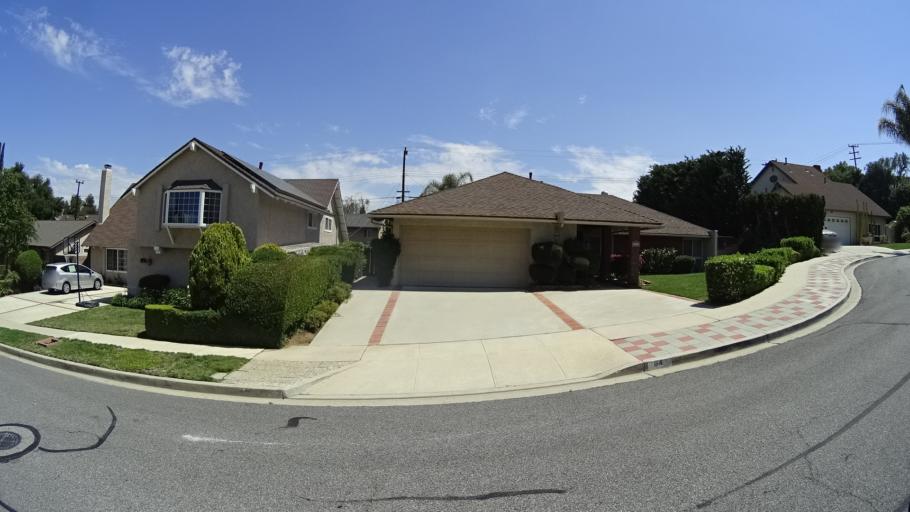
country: US
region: California
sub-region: Ventura County
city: Casa Conejo
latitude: 34.1777
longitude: -118.9186
